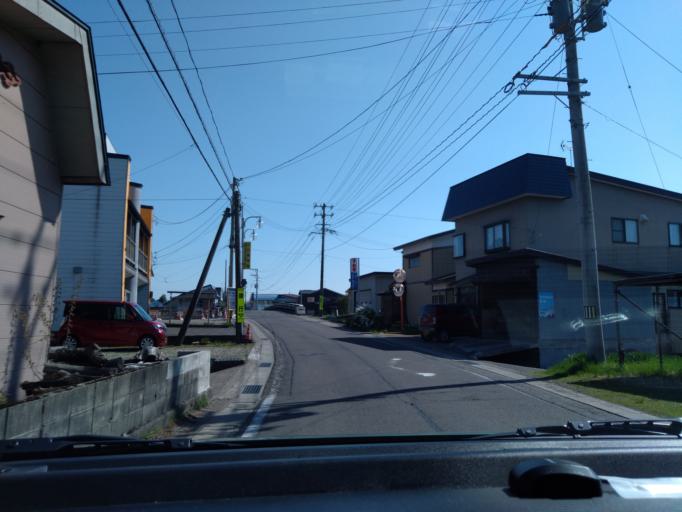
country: JP
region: Akita
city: Kakunodatemachi
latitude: 39.4975
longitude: 140.5941
